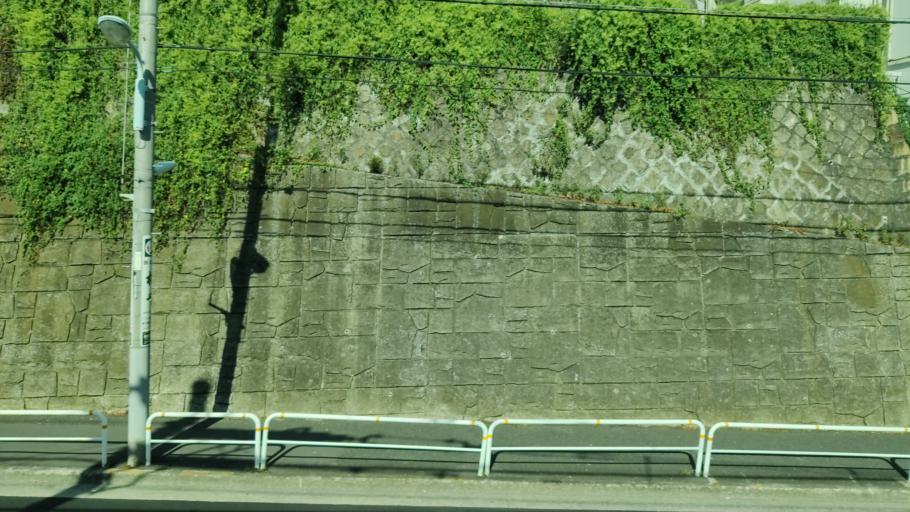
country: JP
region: Tokyo
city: Tokyo
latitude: 35.6298
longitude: 139.7182
